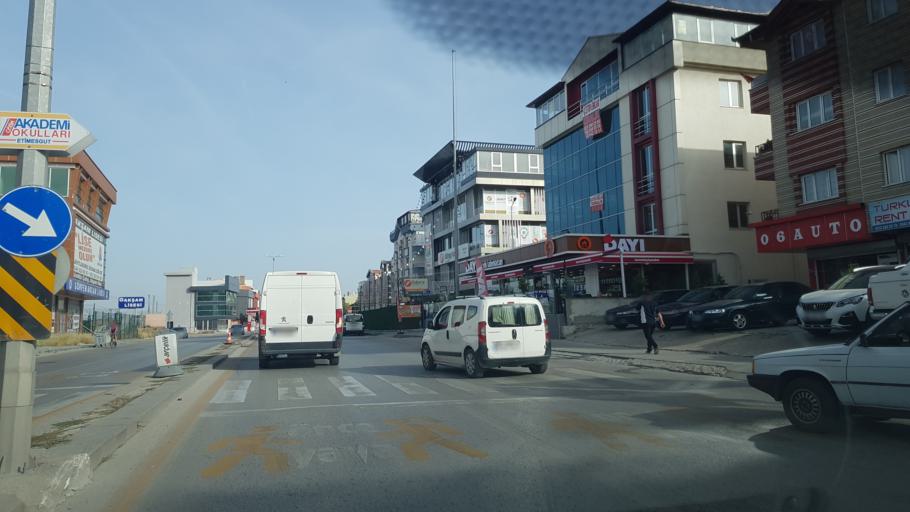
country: TR
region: Ankara
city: Etimesgut
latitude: 39.9525
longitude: 32.6429
